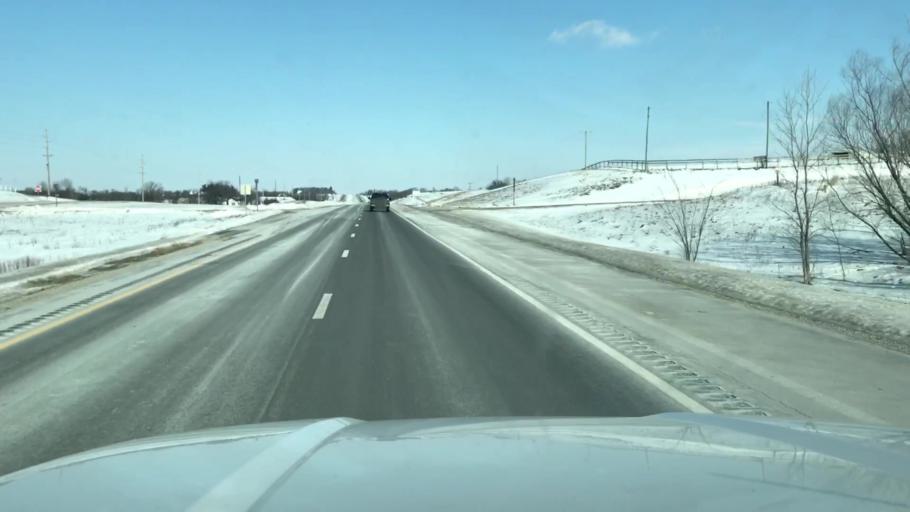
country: US
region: Missouri
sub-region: Nodaway County
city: Maryville
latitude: 40.1851
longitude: -94.8679
